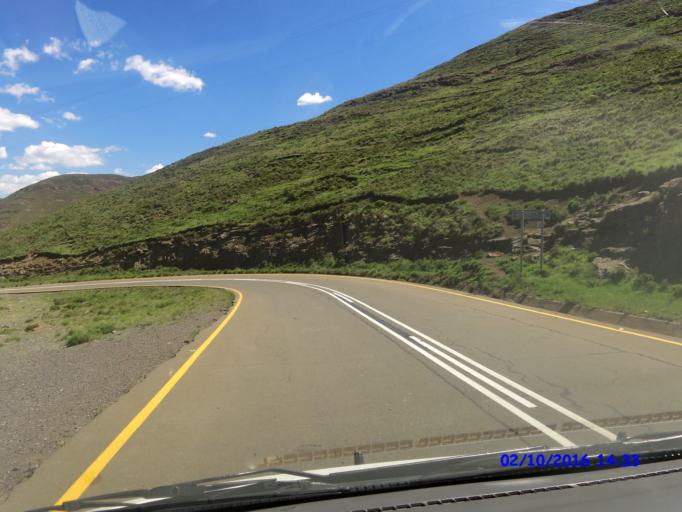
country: LS
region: Maseru
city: Nako
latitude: -29.4856
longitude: 28.0601
